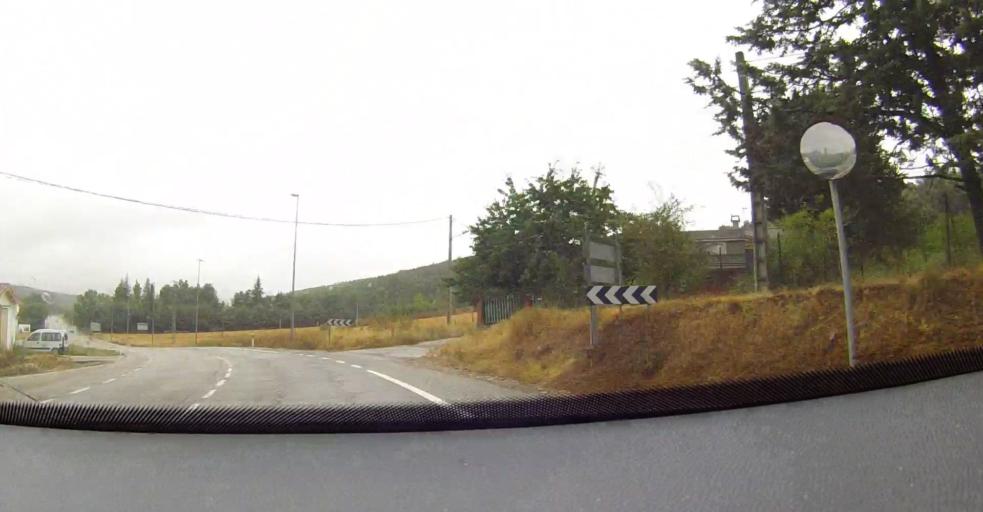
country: ES
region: Castille and Leon
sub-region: Provincia de Palencia
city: Saldana
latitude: 42.5257
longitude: -4.7317
